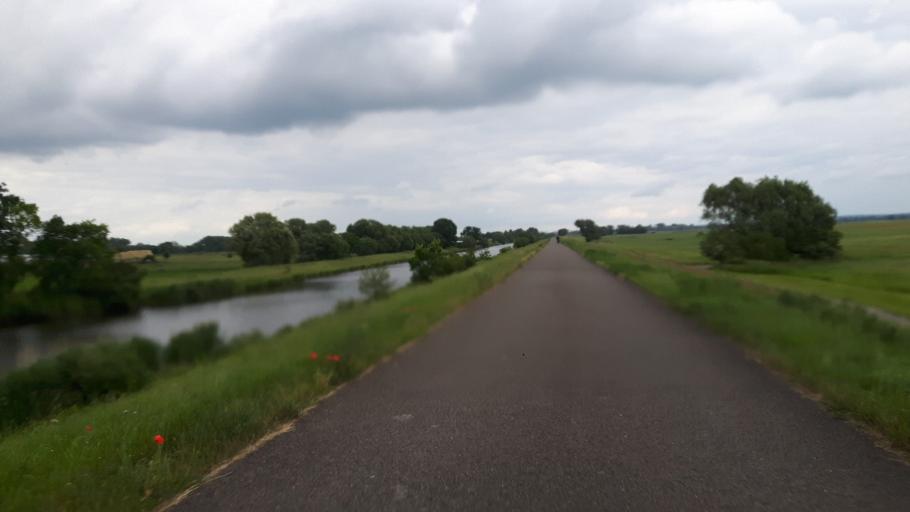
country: DE
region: Brandenburg
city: Meyenburg
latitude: 53.0249
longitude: 14.2461
